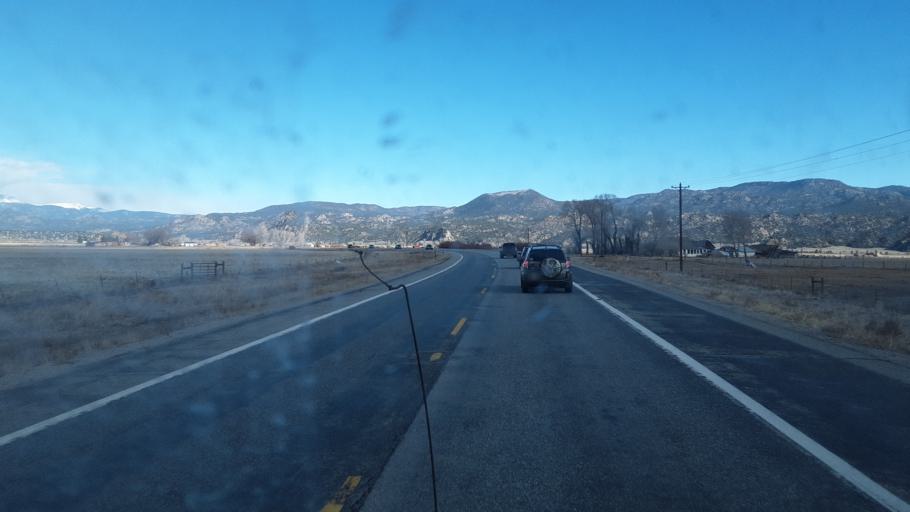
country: US
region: Colorado
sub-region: Chaffee County
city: Buena Vista
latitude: 38.7170
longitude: -106.0869
